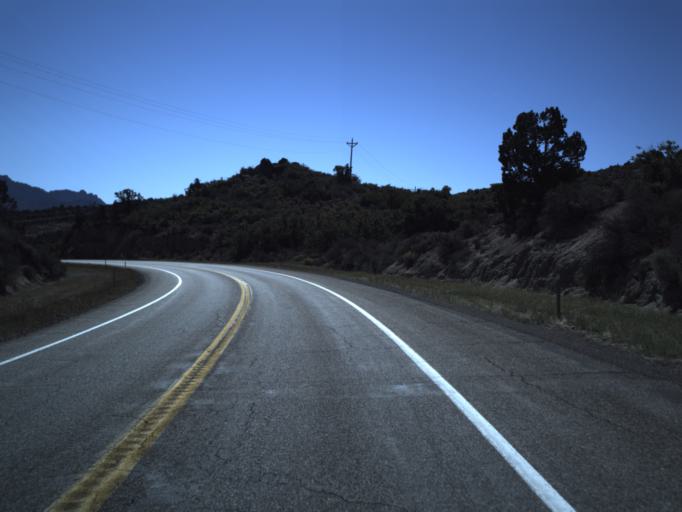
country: US
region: Utah
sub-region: Washington County
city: Enterprise
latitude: 37.4653
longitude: -113.6351
